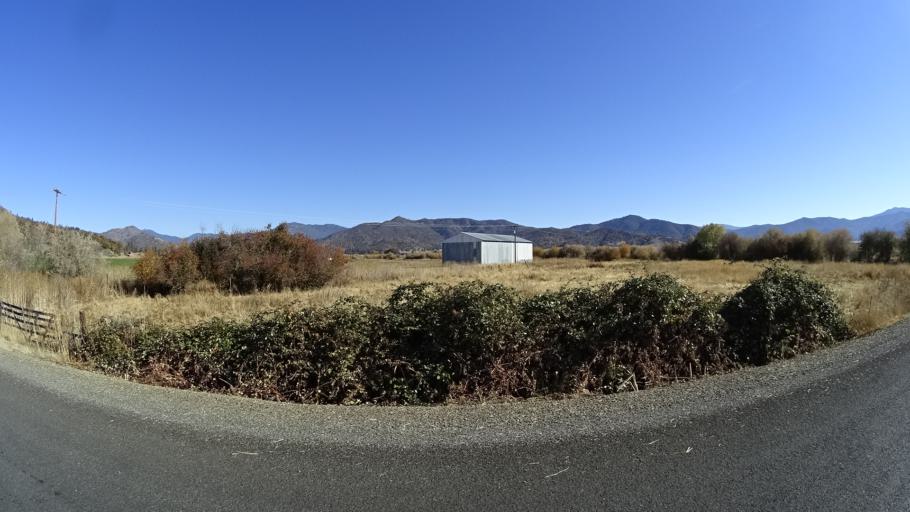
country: US
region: California
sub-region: Siskiyou County
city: Yreka
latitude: 41.5774
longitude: -122.8606
